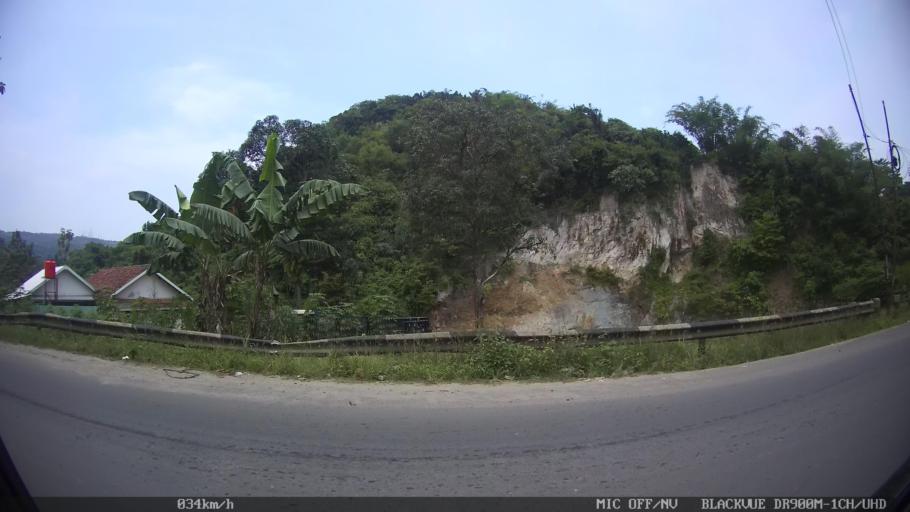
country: ID
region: Lampung
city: Bandarlampung
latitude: -5.4217
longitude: 105.2859
